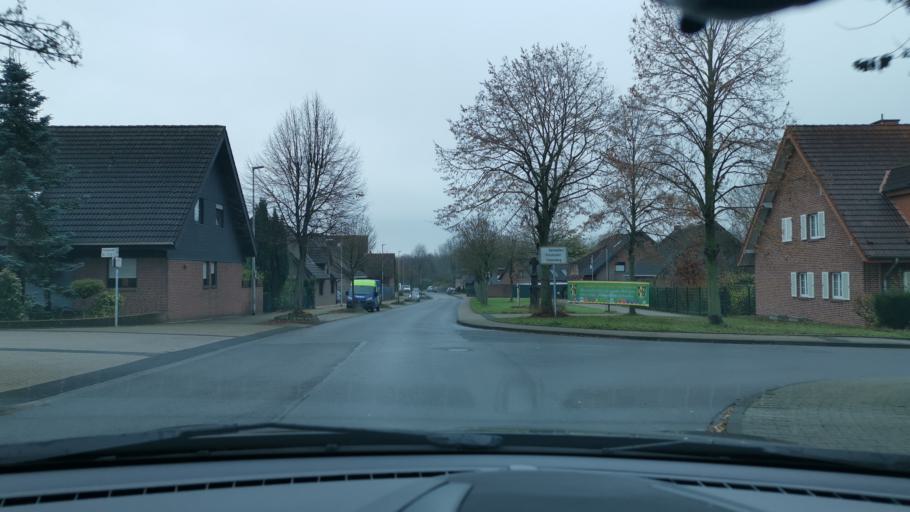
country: DE
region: North Rhine-Westphalia
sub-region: Regierungsbezirk Dusseldorf
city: Juchen
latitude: 51.1069
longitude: 6.5018
